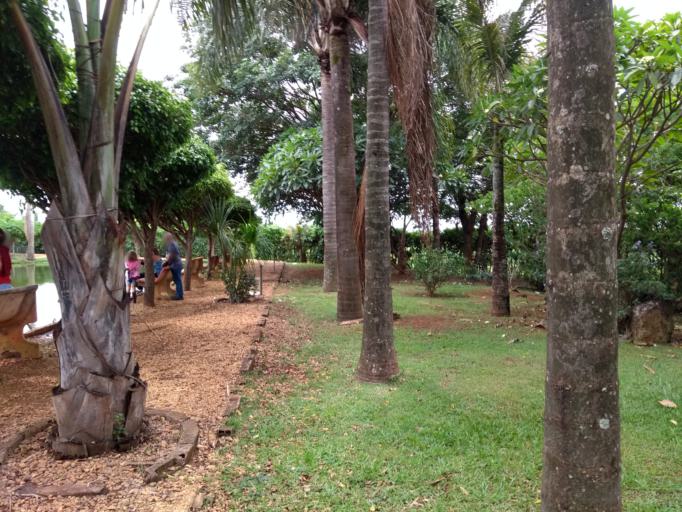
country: BR
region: Federal District
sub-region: Brasilia
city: Brasilia
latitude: -15.9806
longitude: -48.0816
